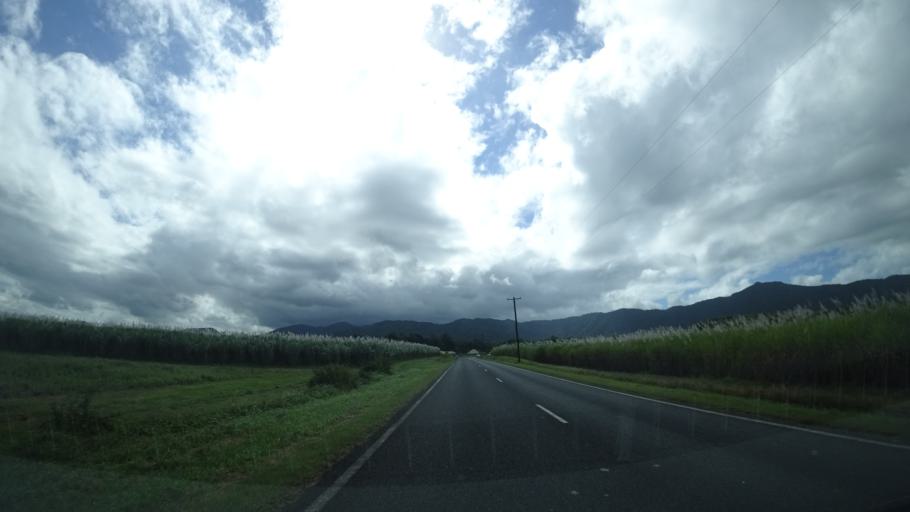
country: AU
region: Queensland
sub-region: Cairns
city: Port Douglas
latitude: -16.2657
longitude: 145.3925
